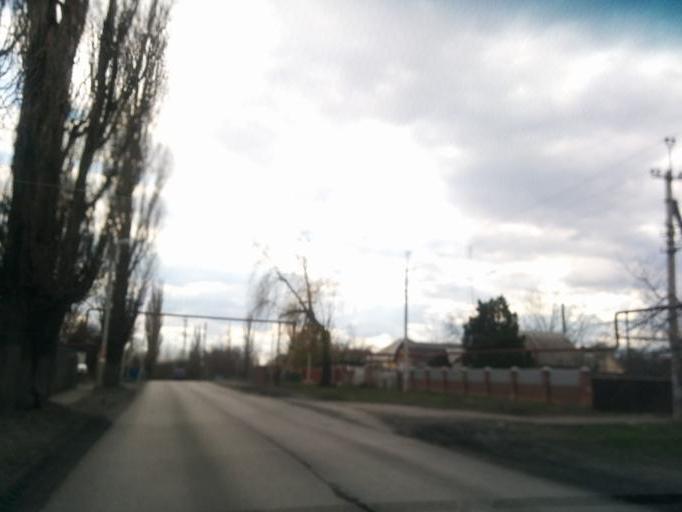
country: RU
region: Rostov
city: Shakhty
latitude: 47.6846
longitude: 40.2863
